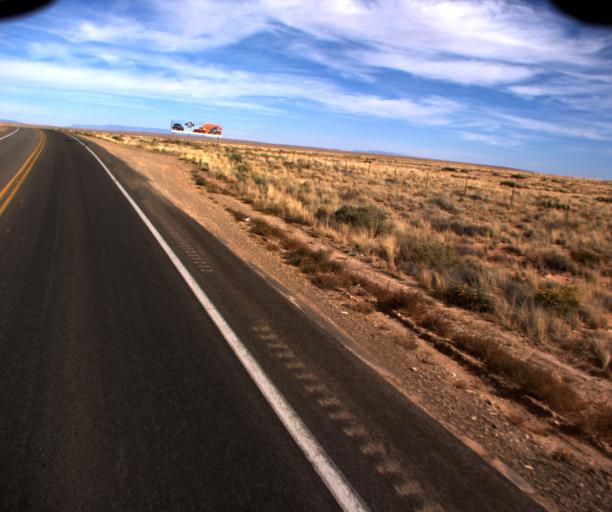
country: US
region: Arizona
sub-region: Navajo County
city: Kayenta
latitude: 36.7290
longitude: -110.1086
